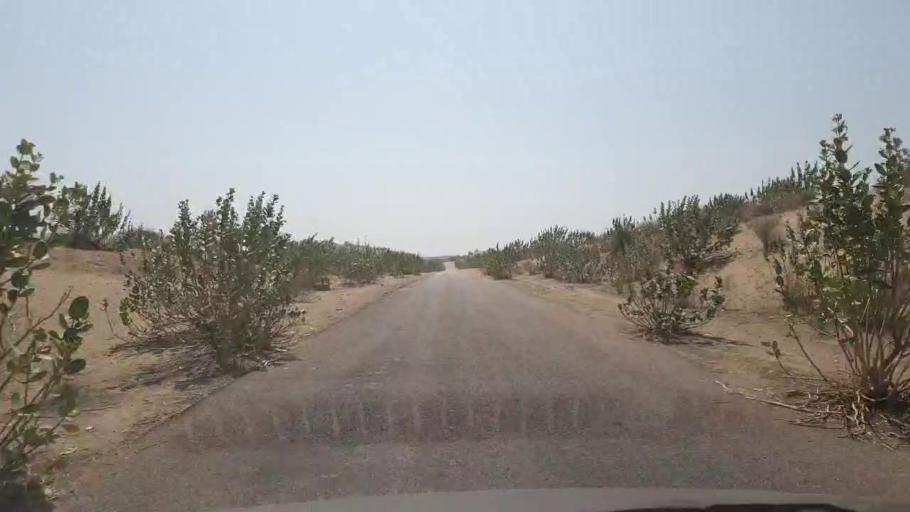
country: PK
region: Sindh
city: Chor
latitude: 25.6570
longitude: 70.1672
